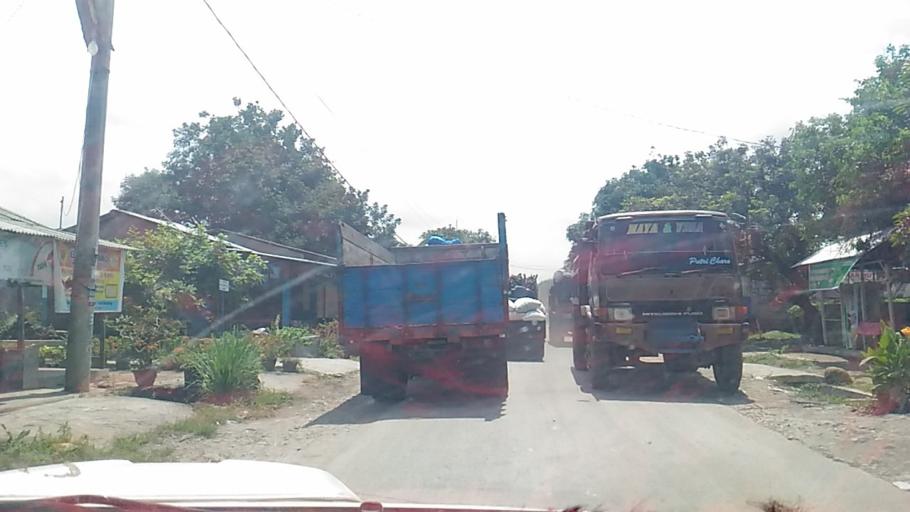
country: ID
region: North Sumatra
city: Sunggal
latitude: 3.5285
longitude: 98.5499
